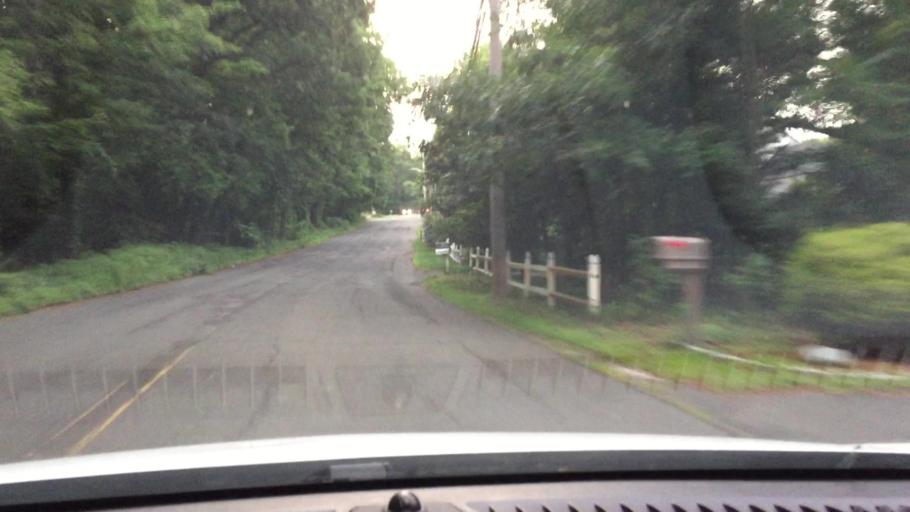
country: US
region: Massachusetts
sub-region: Hampden County
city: Westfield
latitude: 42.1399
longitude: -72.8119
